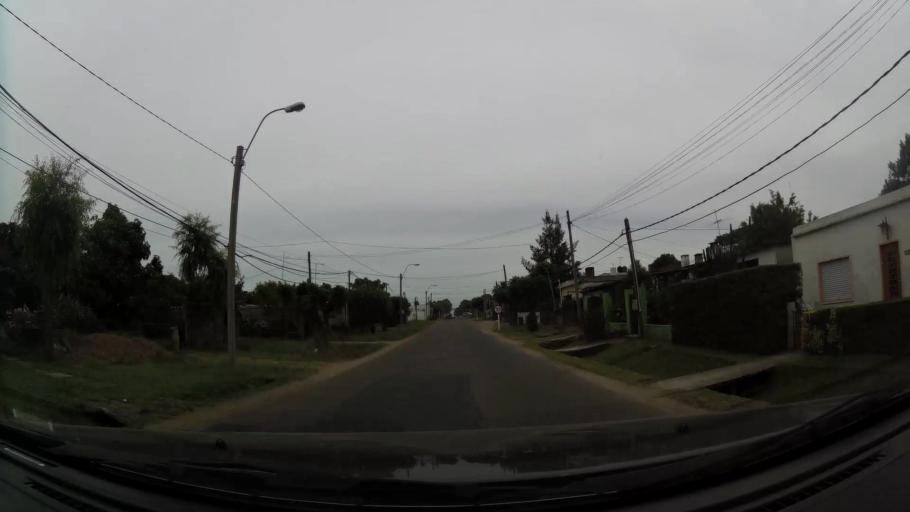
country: UY
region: Canelones
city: Las Piedras
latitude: -34.7373
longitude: -56.2276
